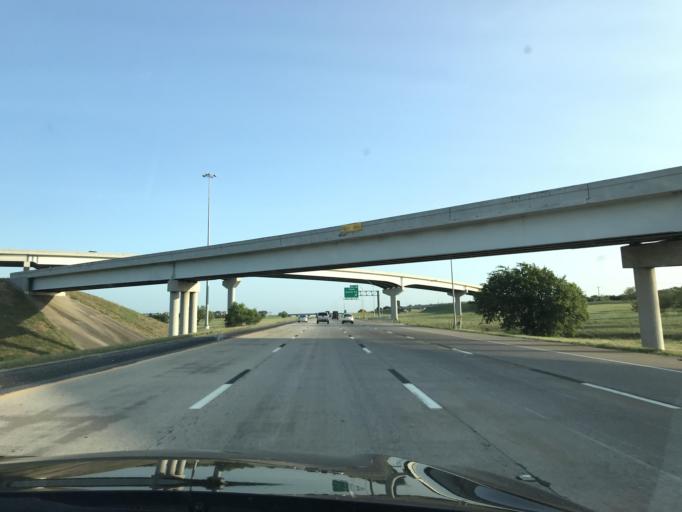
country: US
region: Texas
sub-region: Tarrant County
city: Benbrook
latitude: 32.6930
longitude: -97.4686
